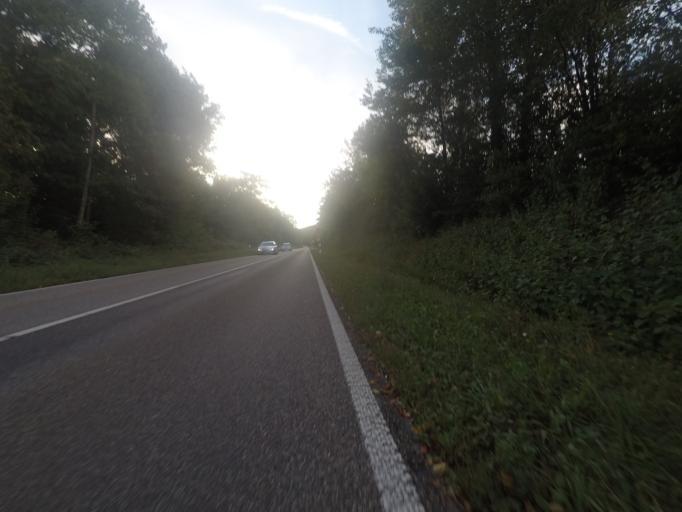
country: DE
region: Baden-Wuerttemberg
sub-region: Karlsruhe Region
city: Ettlingen
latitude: 48.9219
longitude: 8.3854
